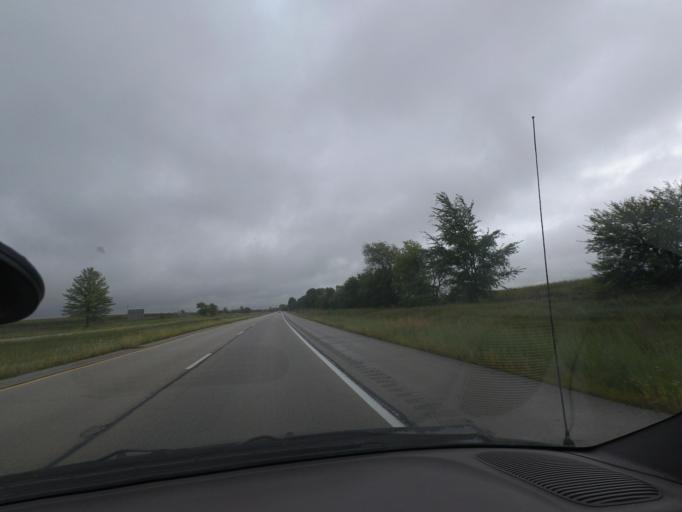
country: US
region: Illinois
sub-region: Piatt County
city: Monticello
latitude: 40.0908
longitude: -88.5138
